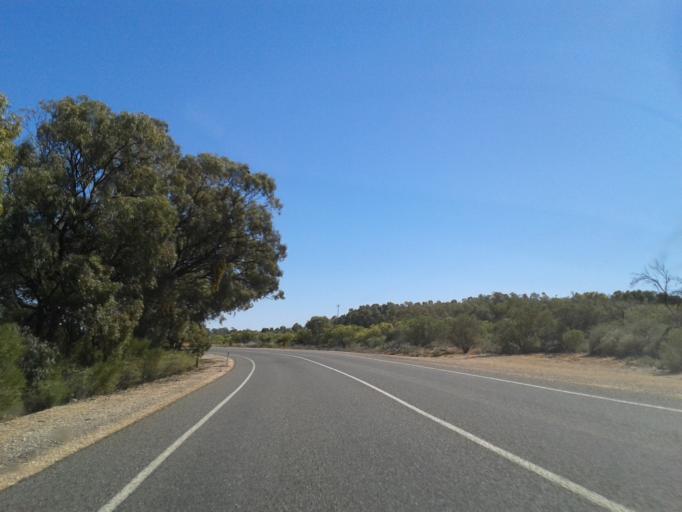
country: AU
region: New South Wales
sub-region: Wentworth
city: Dareton
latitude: -34.1331
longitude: 141.9959
